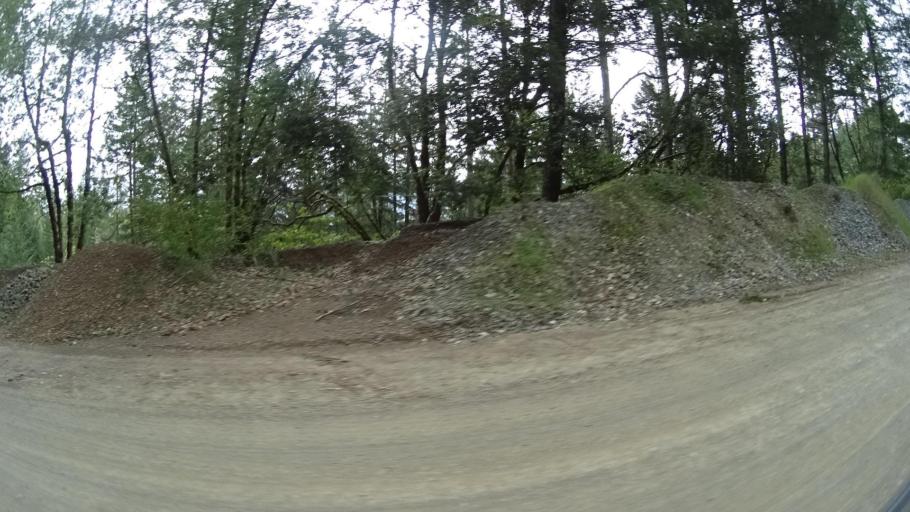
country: US
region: California
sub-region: Humboldt County
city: Redway
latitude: 40.2594
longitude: -123.7676
